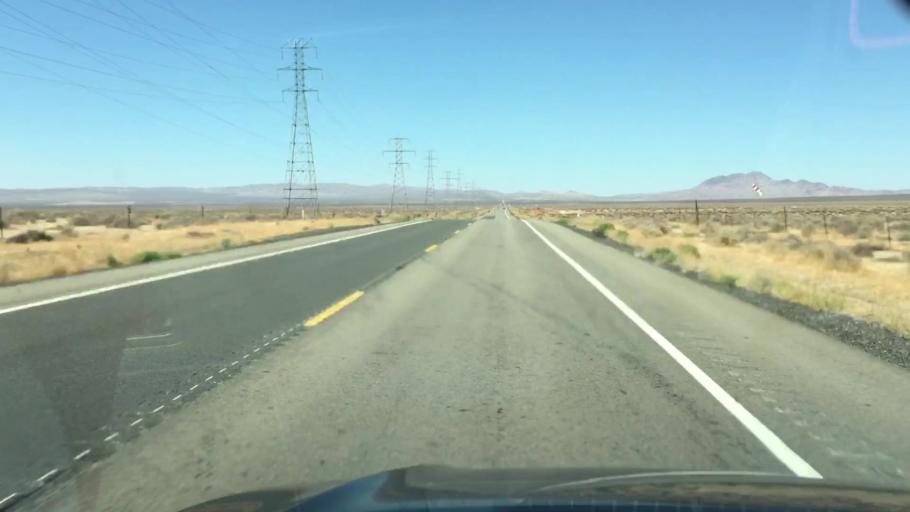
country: US
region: California
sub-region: Kern County
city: Boron
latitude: 35.1675
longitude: -117.5904
